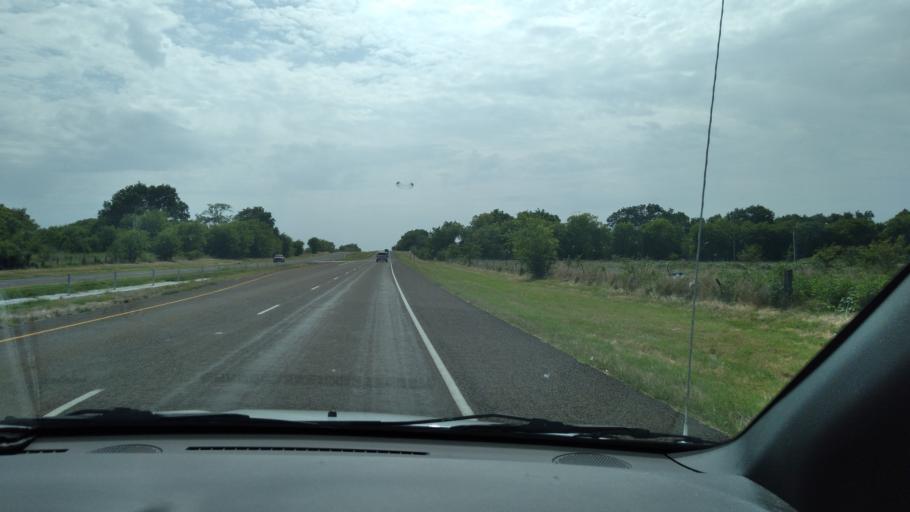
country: US
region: Texas
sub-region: Navarro County
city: Corsicana
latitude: 32.1067
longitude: -96.3783
